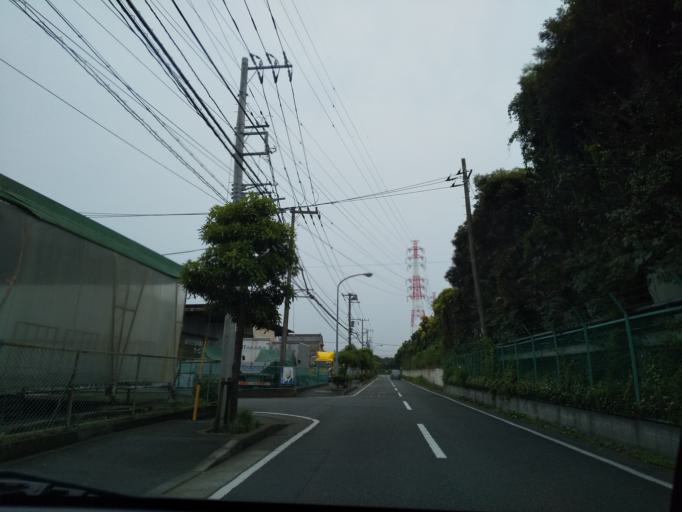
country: JP
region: Kanagawa
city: Minami-rinkan
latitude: 35.4607
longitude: 139.4294
